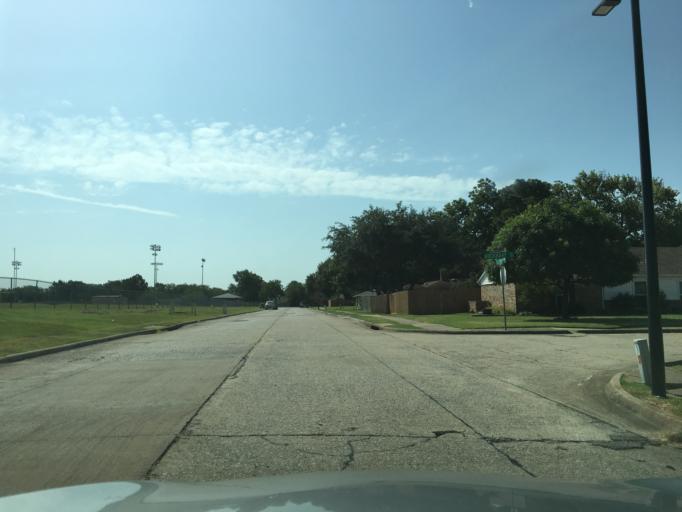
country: US
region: Texas
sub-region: Dallas County
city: Garland
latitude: 32.8717
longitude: -96.6228
